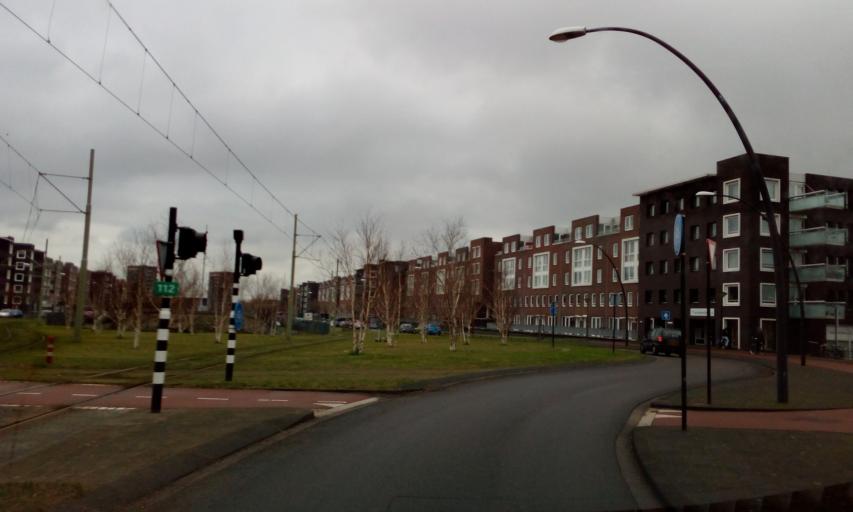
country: NL
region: South Holland
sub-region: Gemeente Rijswijk
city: Rijswijk
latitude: 52.0237
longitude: 4.2927
